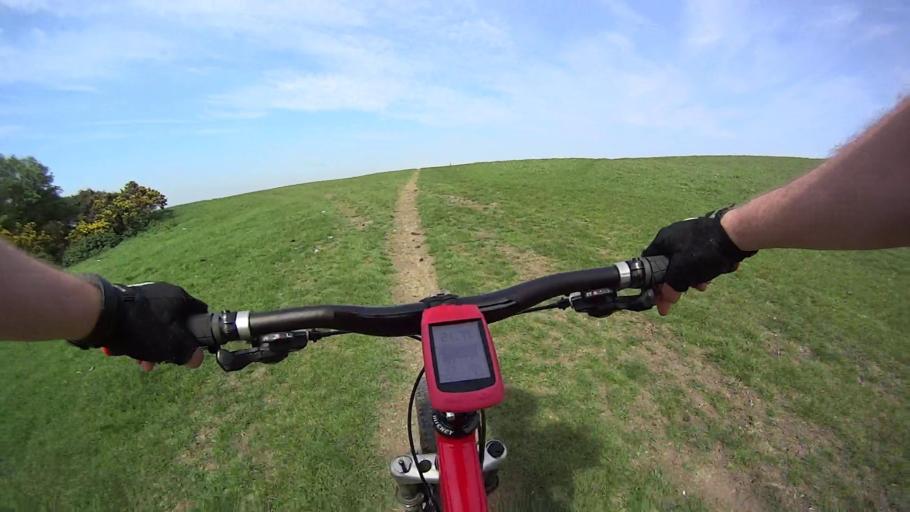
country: GB
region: England
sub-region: East Sussex
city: Hailsham
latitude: 50.8065
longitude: 0.1951
